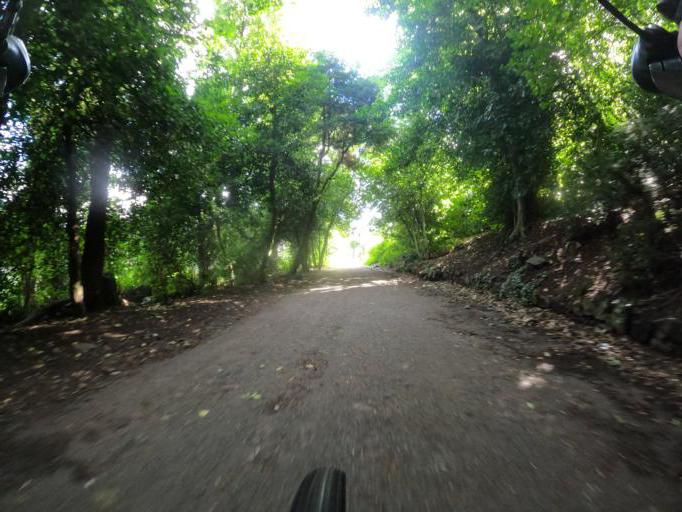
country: GB
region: Scotland
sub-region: Edinburgh
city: Colinton
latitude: 55.9565
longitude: -3.2492
